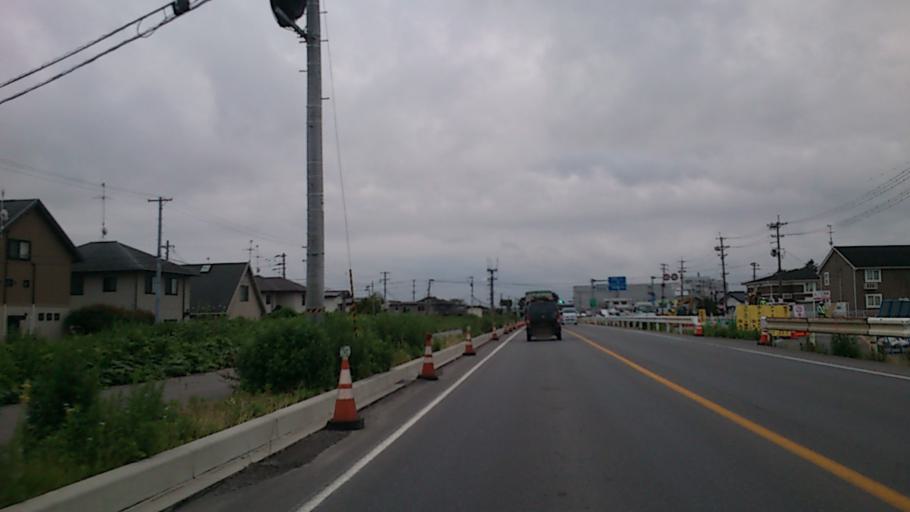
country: JP
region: Fukushima
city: Sukagawa
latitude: 37.2574
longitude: 140.3456
